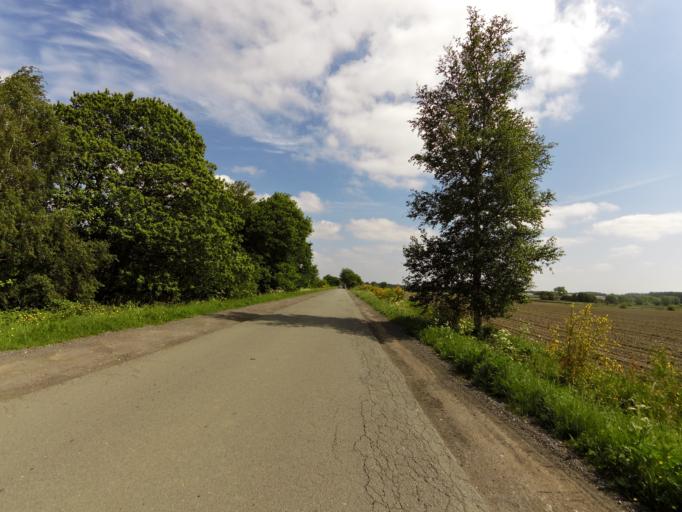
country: BE
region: Flanders
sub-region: Provincie Oost-Vlaanderen
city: Knesselare
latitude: 51.1206
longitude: 3.3837
